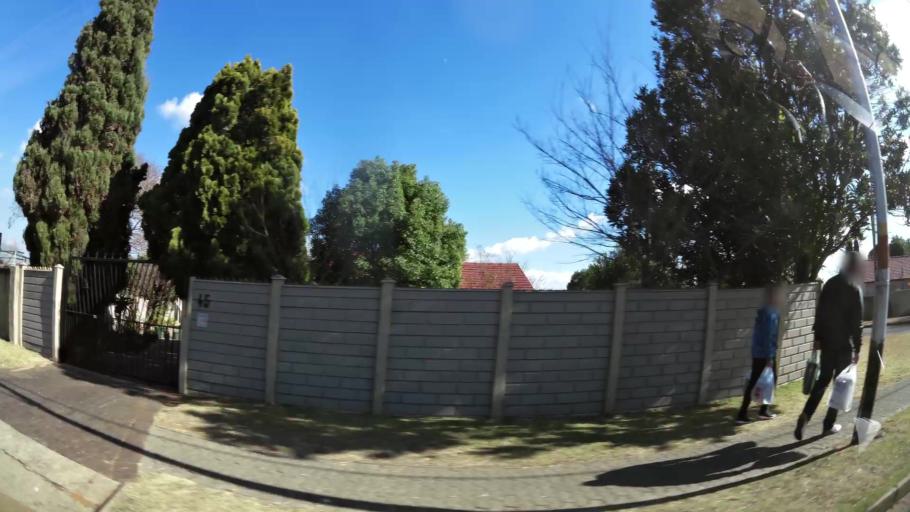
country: ZA
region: Gauteng
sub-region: City of Johannesburg Metropolitan Municipality
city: Roodepoort
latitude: -26.1386
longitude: 27.8286
